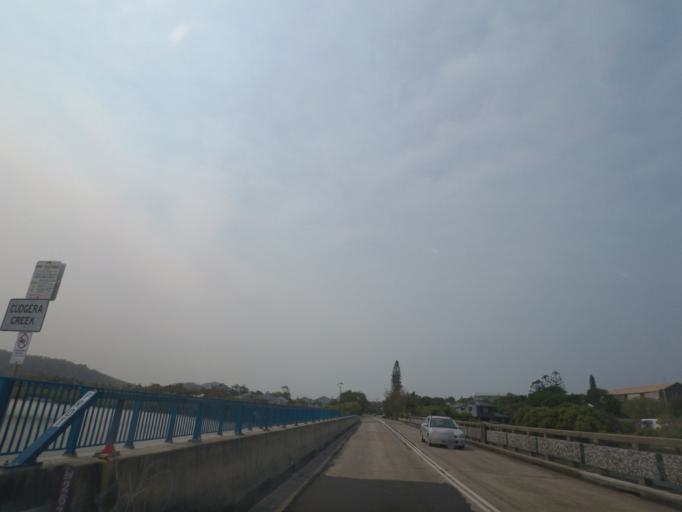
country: AU
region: New South Wales
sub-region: Tweed
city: Pottsville Beach
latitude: -28.3589
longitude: 153.5740
